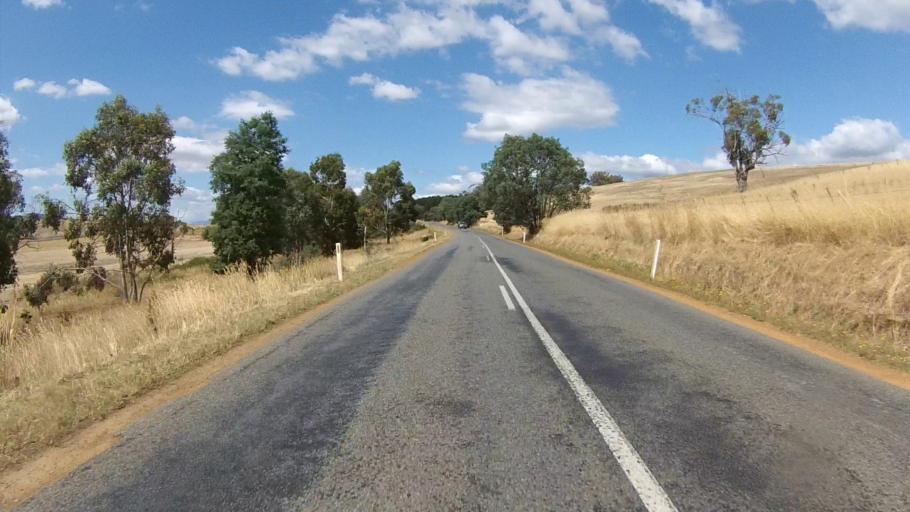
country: AU
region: Tasmania
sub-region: Derwent Valley
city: New Norfolk
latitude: -42.6859
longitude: 146.8697
